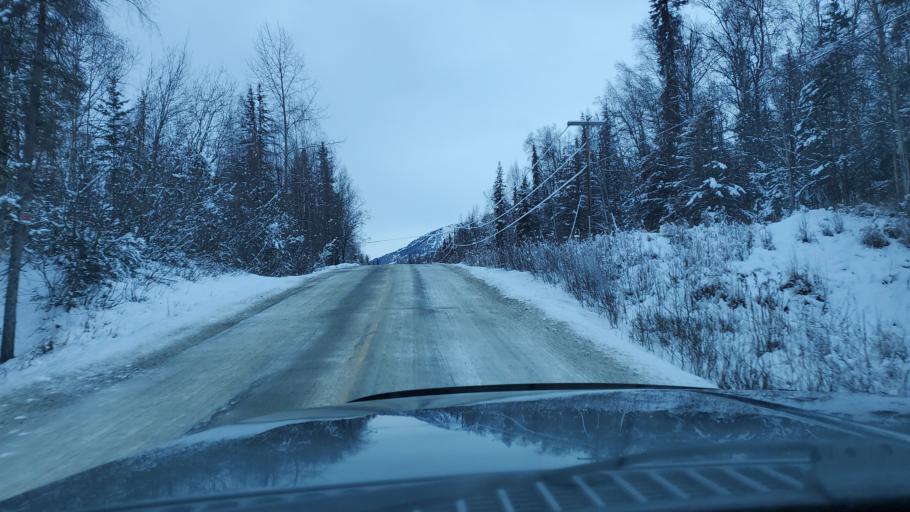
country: US
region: Alaska
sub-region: Matanuska-Susitna Borough
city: Lakes
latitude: 61.6933
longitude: -149.3160
